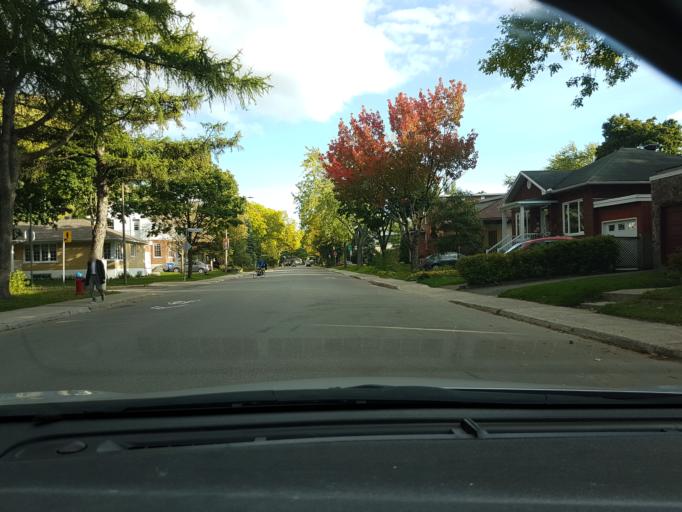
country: CA
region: Quebec
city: Quebec
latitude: 46.7910
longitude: -71.2557
